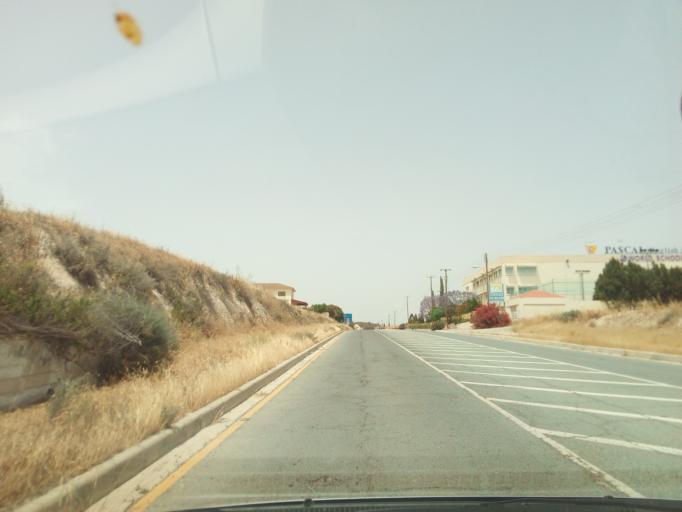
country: CY
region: Larnaka
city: Aradippou
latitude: 34.9520
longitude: 33.5692
